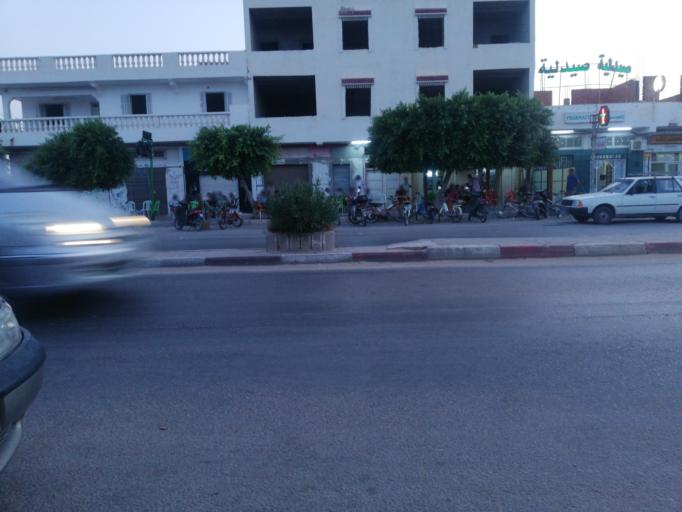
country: TN
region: Qabis
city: Matmata
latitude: 33.6151
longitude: 10.2906
